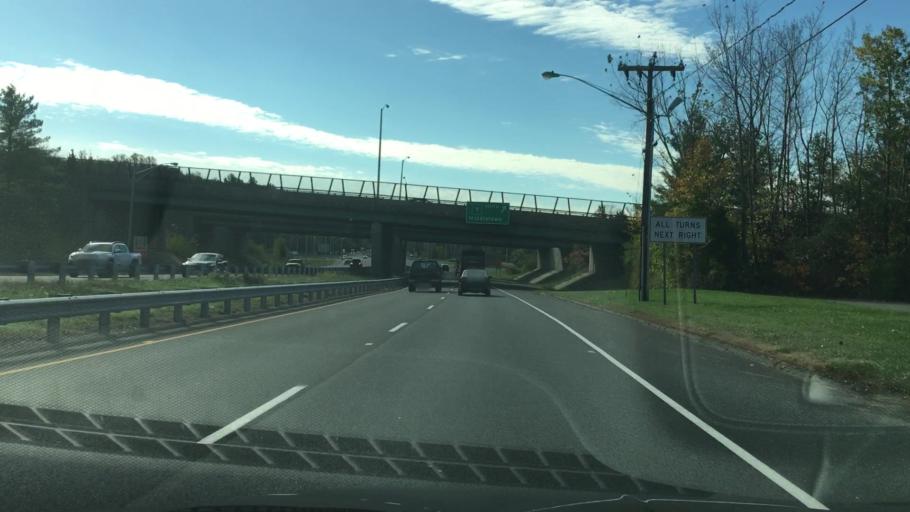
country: US
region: Connecticut
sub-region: Hartford County
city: Kensington
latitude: 41.6262
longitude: -72.7407
